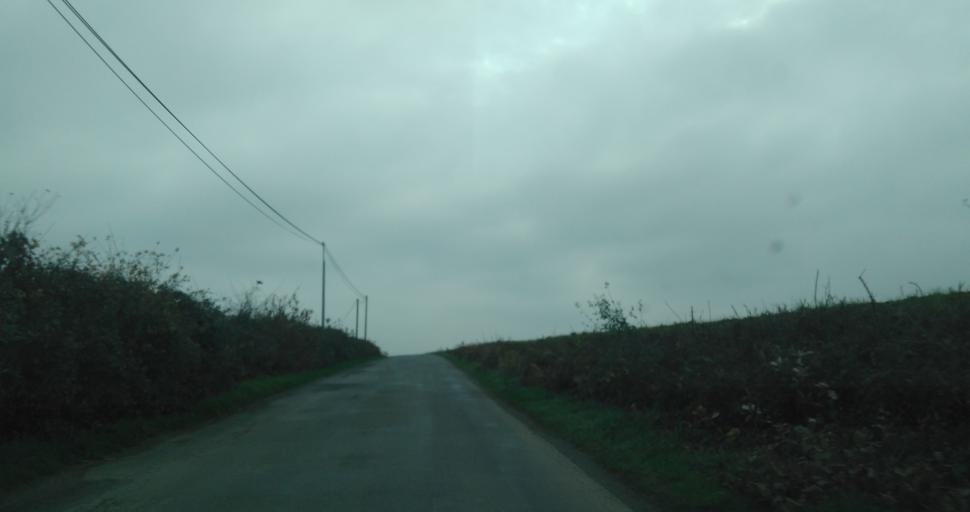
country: FR
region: Brittany
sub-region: Departement d'Ille-et-Vilaine
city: Iffendic
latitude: 48.0954
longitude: -2.0643
